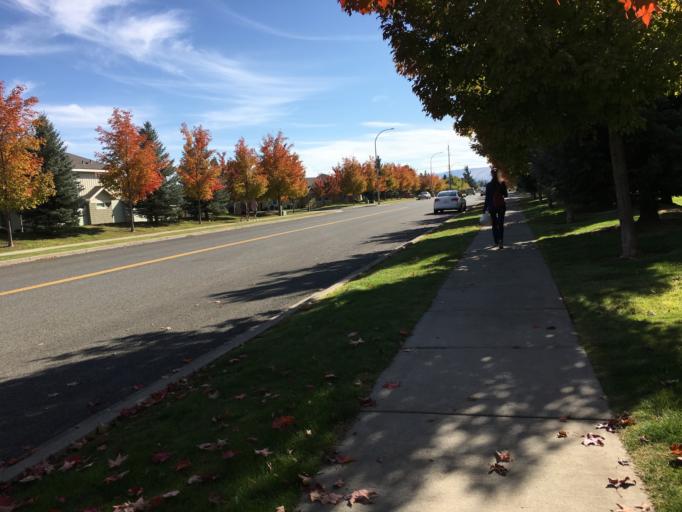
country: US
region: Washington
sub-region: Kittitas County
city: Ellensburg
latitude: 47.0159
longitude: -120.5320
